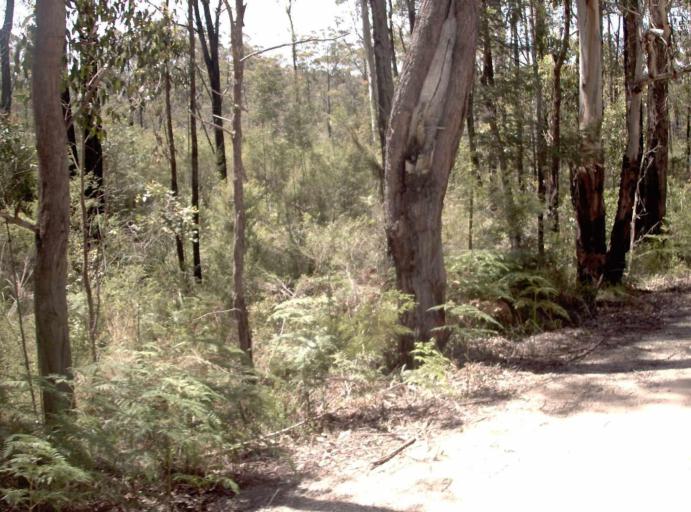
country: AU
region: New South Wales
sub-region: Bombala
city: Bombala
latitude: -37.6322
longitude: 148.8779
